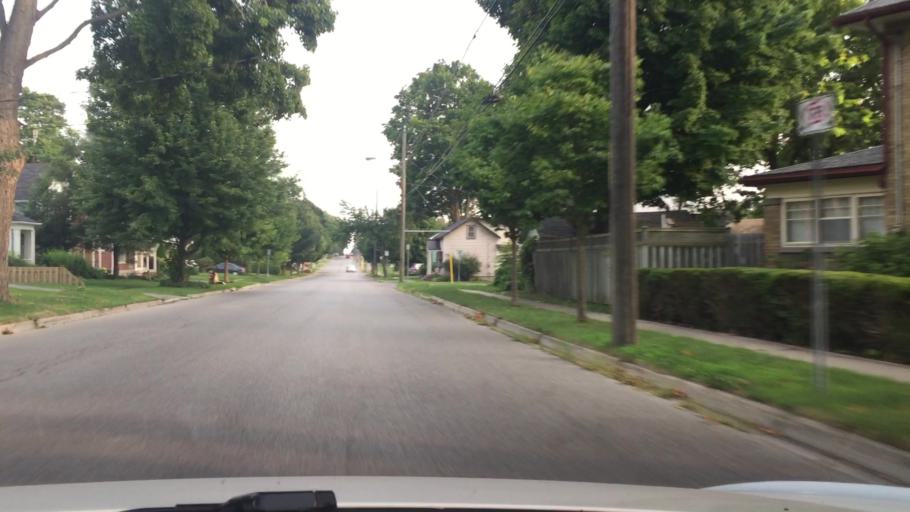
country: CA
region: Ontario
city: Cobourg
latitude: 43.9583
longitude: -78.2898
